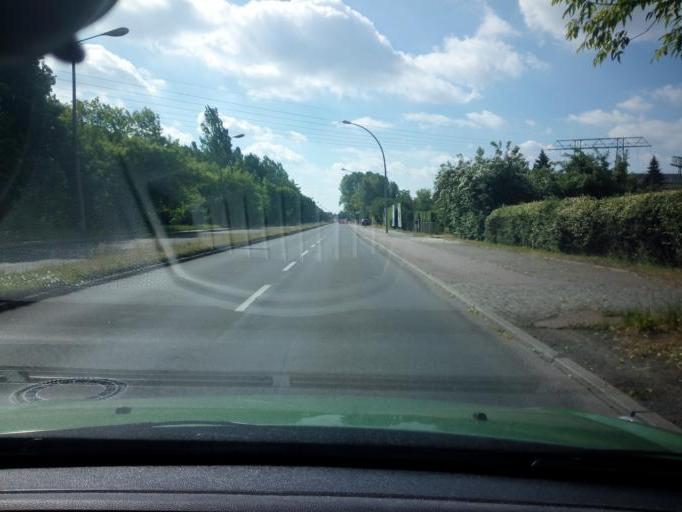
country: DE
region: Berlin
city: Oberschoneweide
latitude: 52.4765
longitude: 13.5059
